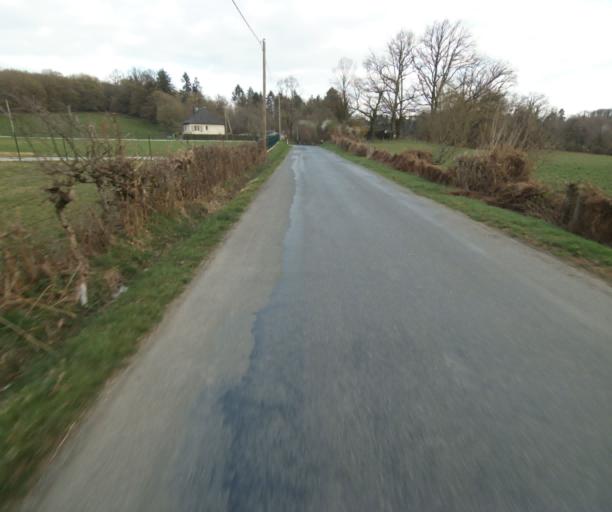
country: FR
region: Limousin
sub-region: Departement de la Correze
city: Saint-Clement
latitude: 45.3598
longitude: 1.6287
